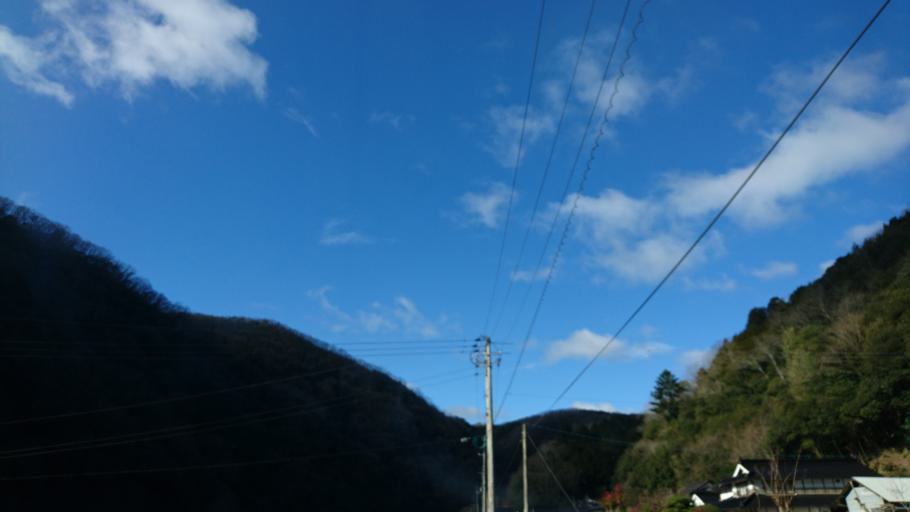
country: JP
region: Okayama
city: Takahashi
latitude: 34.8614
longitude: 133.5685
